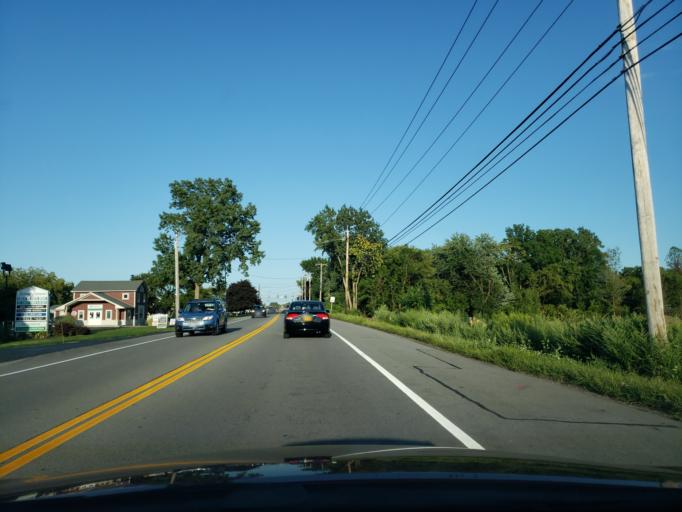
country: US
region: New York
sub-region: Monroe County
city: Webster
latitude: 43.2039
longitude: -77.4872
